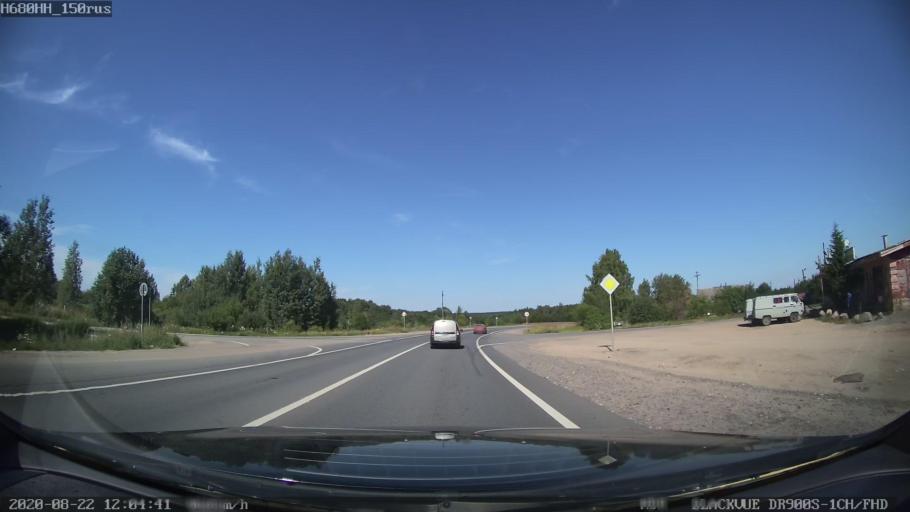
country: RU
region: Tverskaya
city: Rameshki
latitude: 57.2698
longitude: 36.0716
